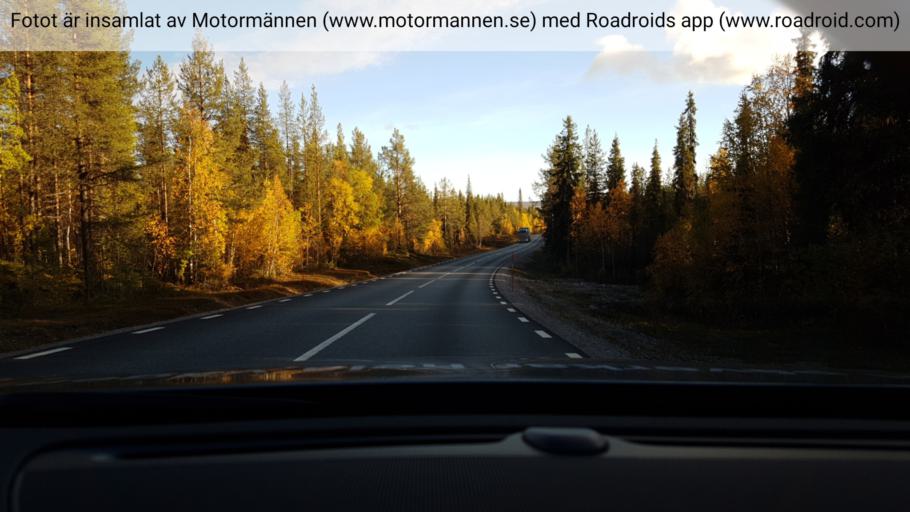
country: SE
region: Norrbotten
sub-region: Jokkmokks Kommun
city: Jokkmokk
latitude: 66.9310
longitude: 19.8220
